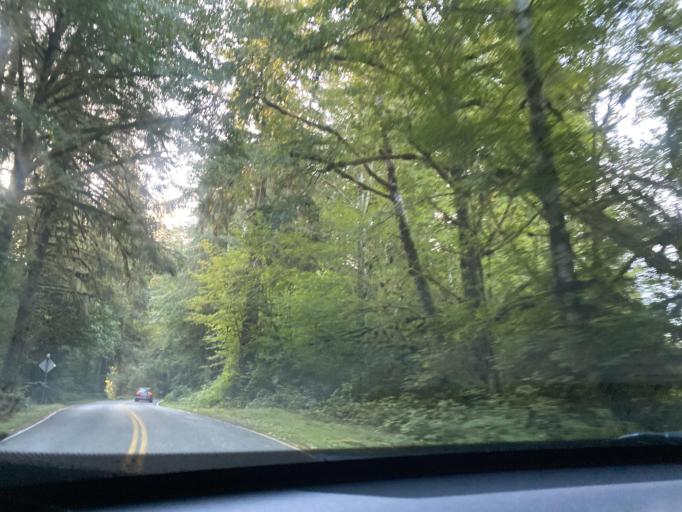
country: US
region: Washington
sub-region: Clallam County
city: Forks
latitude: 47.8190
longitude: -124.1749
